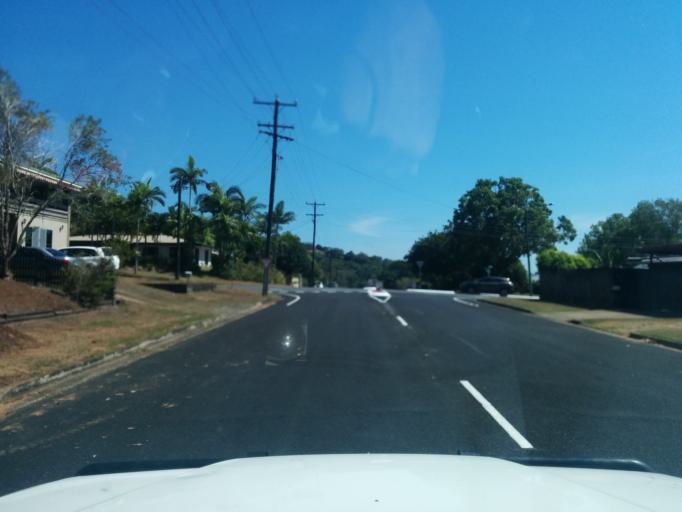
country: AU
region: Queensland
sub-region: Cairns
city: Woree
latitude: -16.9596
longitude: 145.7257
